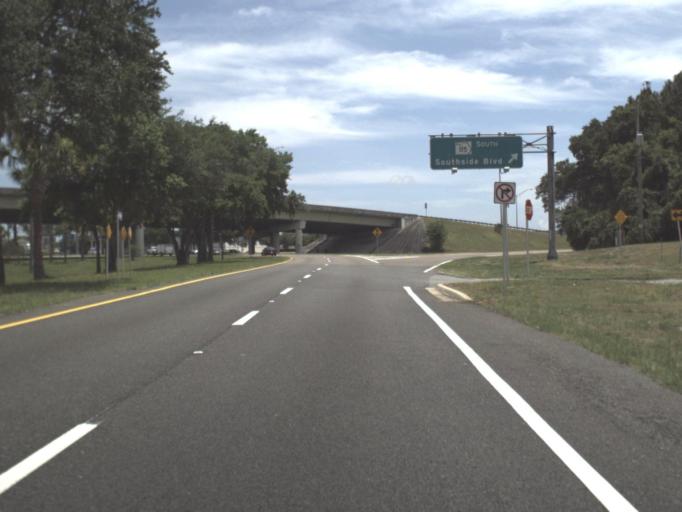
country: US
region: Florida
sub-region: Duval County
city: Jacksonville
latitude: 30.3235
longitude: -81.5609
